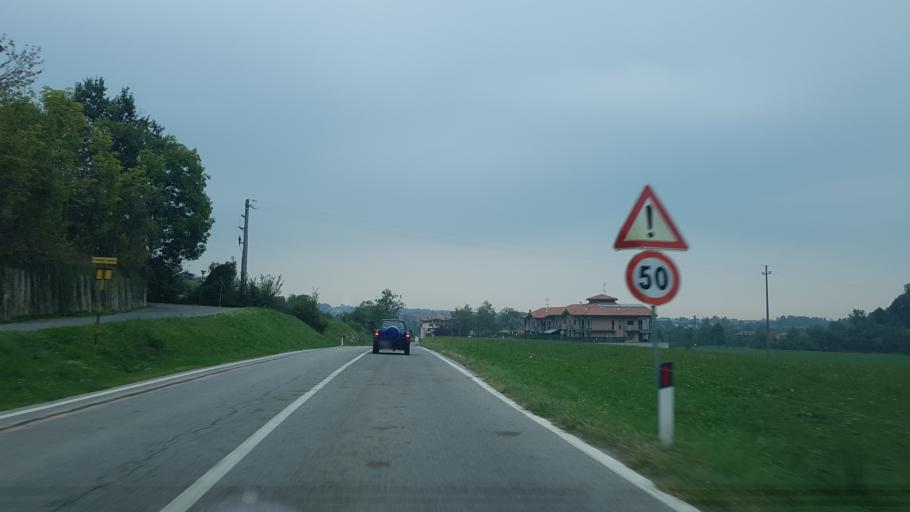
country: IT
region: Piedmont
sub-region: Provincia di Cuneo
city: Villanova Mondovi
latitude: 44.3351
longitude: 7.7810
